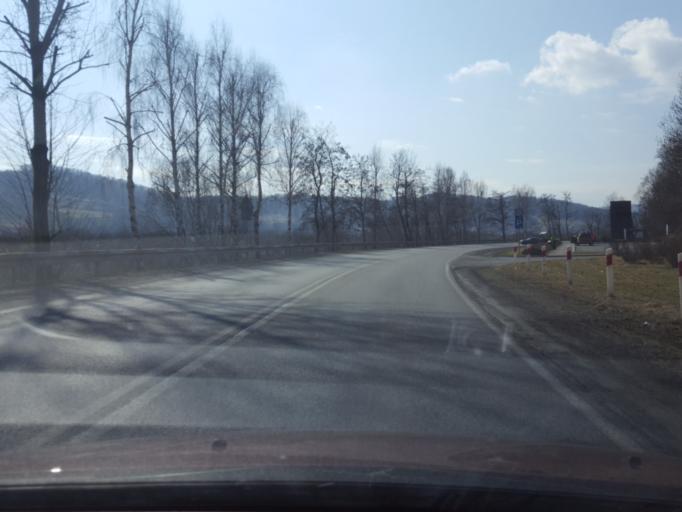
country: PL
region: Lesser Poland Voivodeship
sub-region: Powiat nowosadecki
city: Lososina Dolna
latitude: 49.6972
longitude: 20.6604
